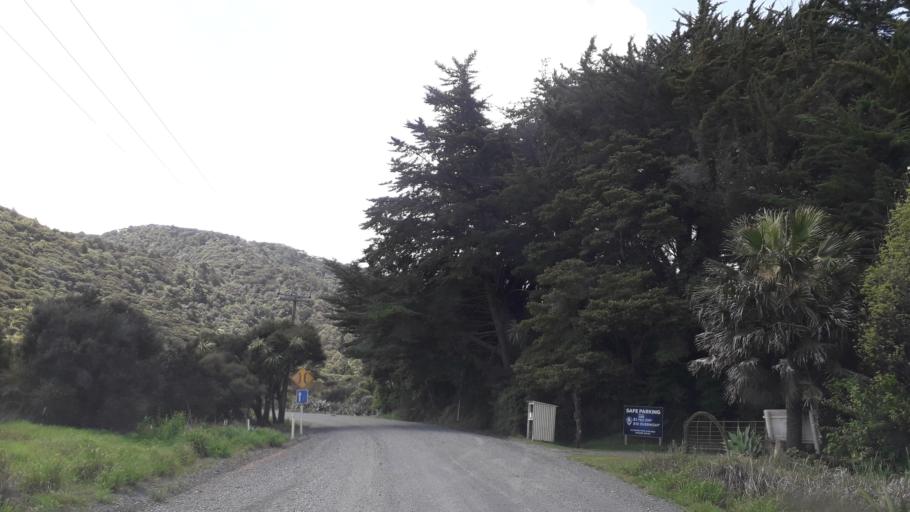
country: NZ
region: Northland
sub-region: Far North District
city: Paihia
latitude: -35.2571
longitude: 174.2665
